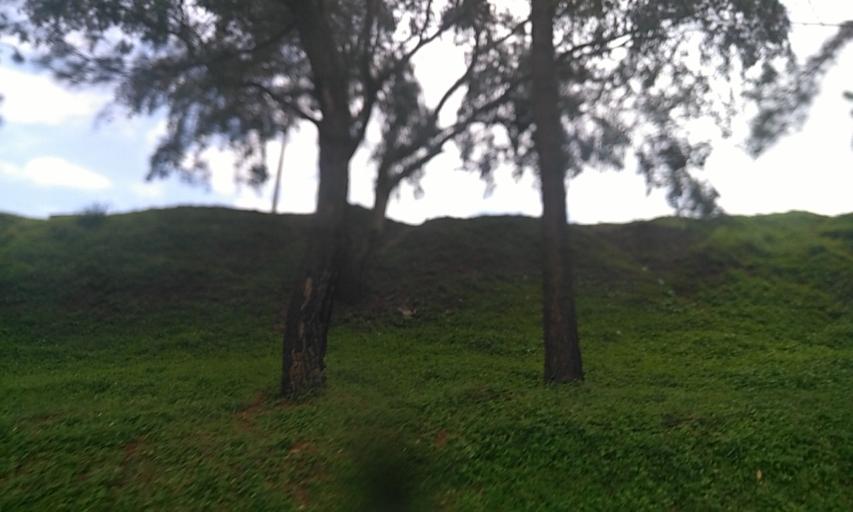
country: UG
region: Central Region
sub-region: Kampala District
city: Kampala
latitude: 0.3258
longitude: 32.5918
